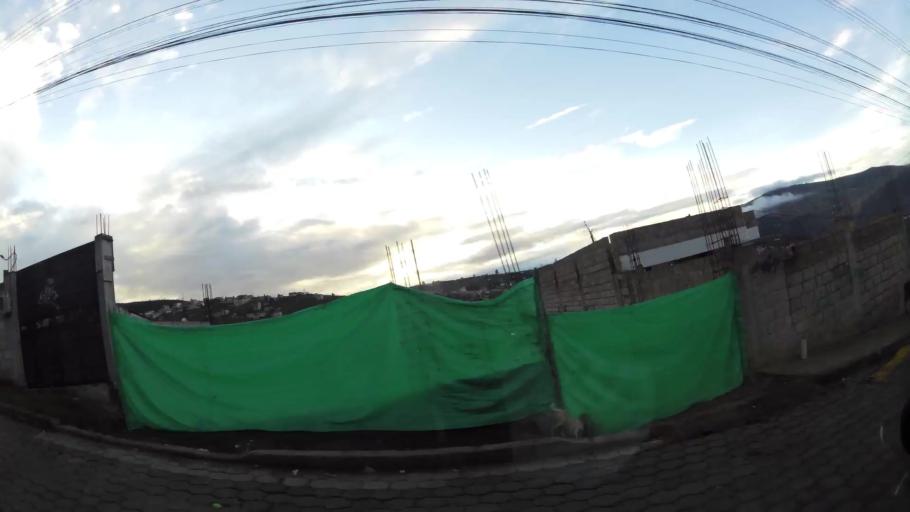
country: EC
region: Pichincha
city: Quito
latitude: -0.0982
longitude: -78.5192
